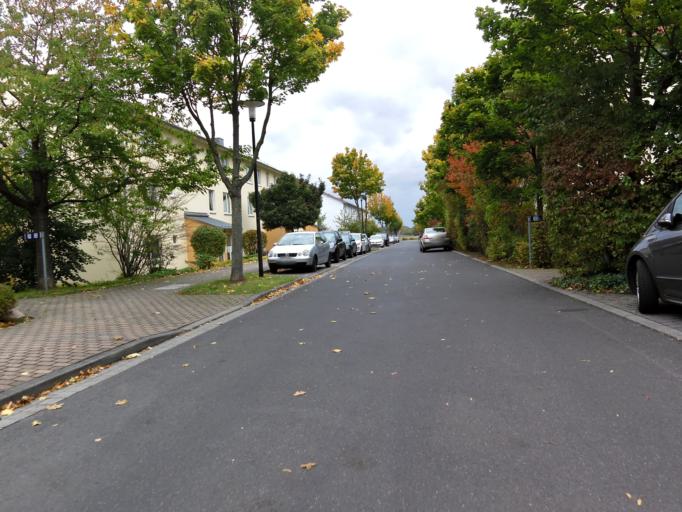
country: DE
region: Saxony
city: Grossposna
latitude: 51.3120
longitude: 12.4566
